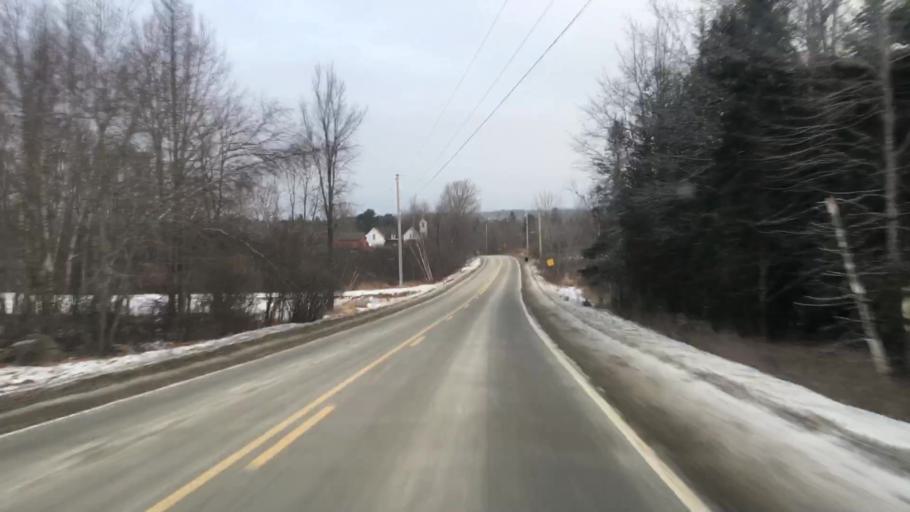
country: US
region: Maine
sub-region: Hancock County
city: Franklin
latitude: 44.6847
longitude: -68.3507
